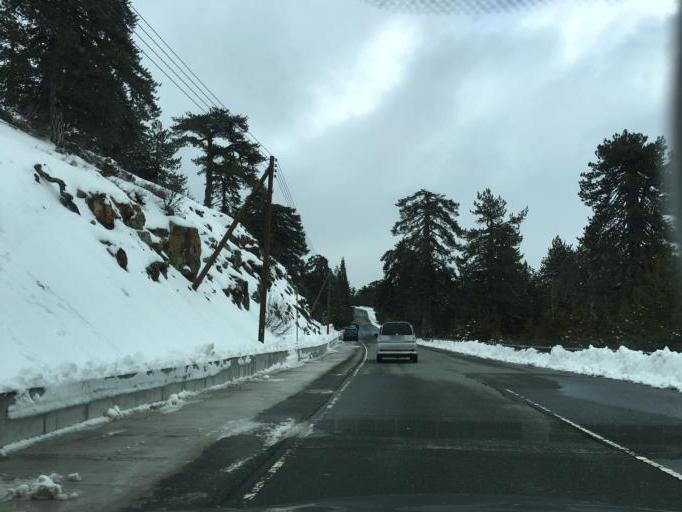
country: CY
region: Lefkosia
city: Kakopetria
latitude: 34.9362
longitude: 32.8708
